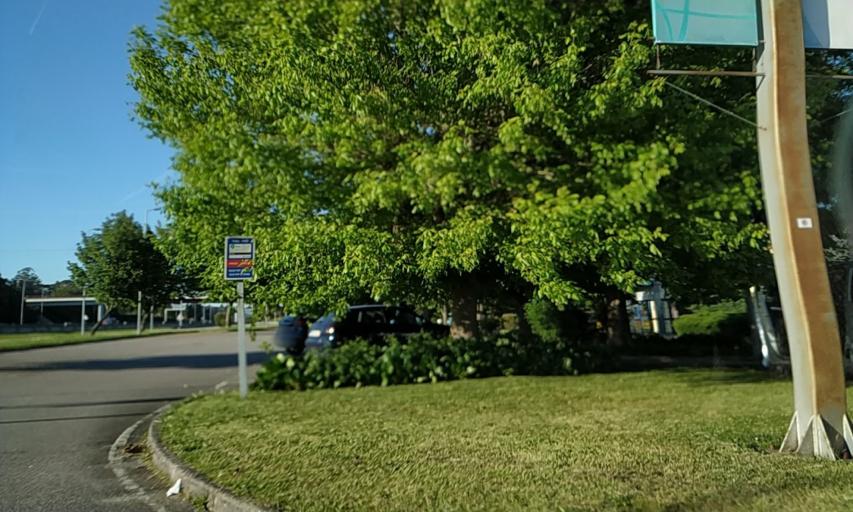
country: PT
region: Porto
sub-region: Trofa
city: Sao Romao do Coronado
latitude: 41.2633
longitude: -8.5634
